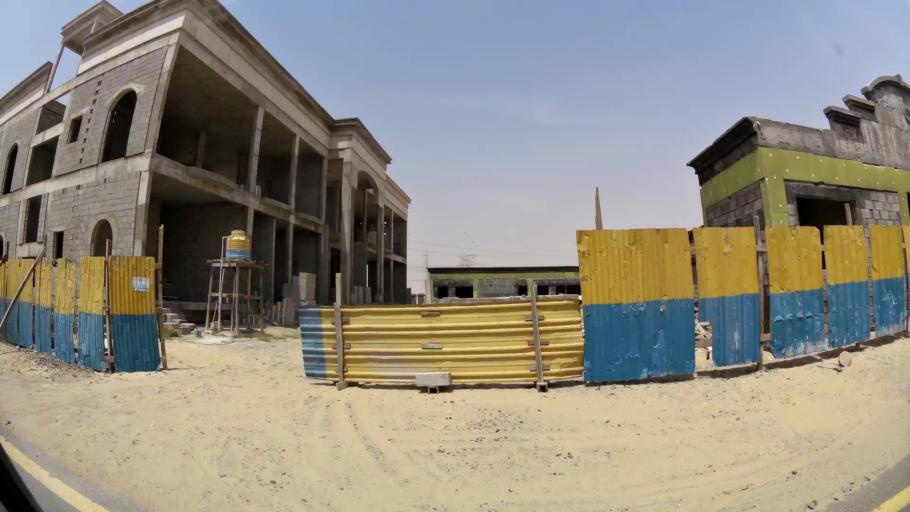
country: AE
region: Ash Shariqah
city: Sharjah
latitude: 25.2523
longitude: 55.5096
